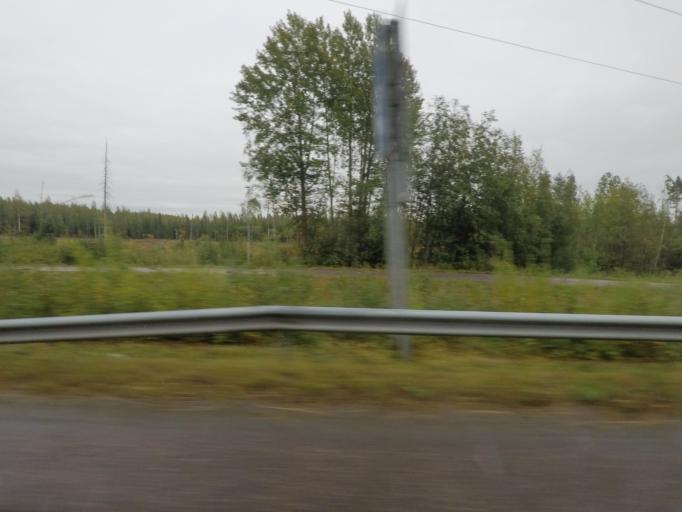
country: FI
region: Northern Savo
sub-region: Varkaus
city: Leppaevirta
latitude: 62.4779
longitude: 27.7718
